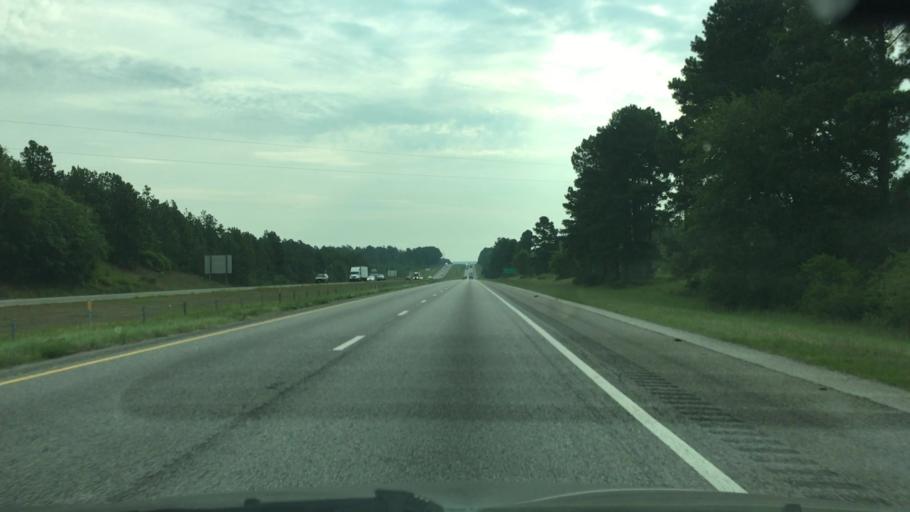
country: US
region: South Carolina
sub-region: Aiken County
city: Aiken
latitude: 33.6716
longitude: -81.6595
